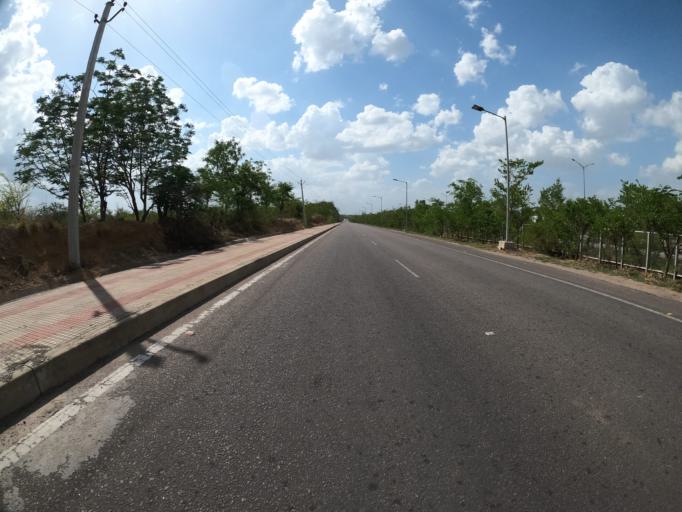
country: IN
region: Telangana
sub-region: Hyderabad
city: Hyderabad
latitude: 17.3628
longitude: 78.3528
